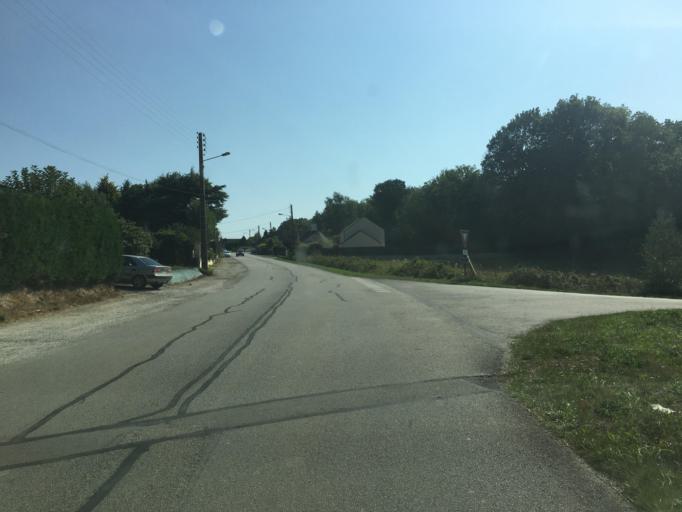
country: FR
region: Brittany
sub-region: Departement des Cotes-d'Armor
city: Mur-de-Bretagne
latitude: 48.2008
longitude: -2.9955
